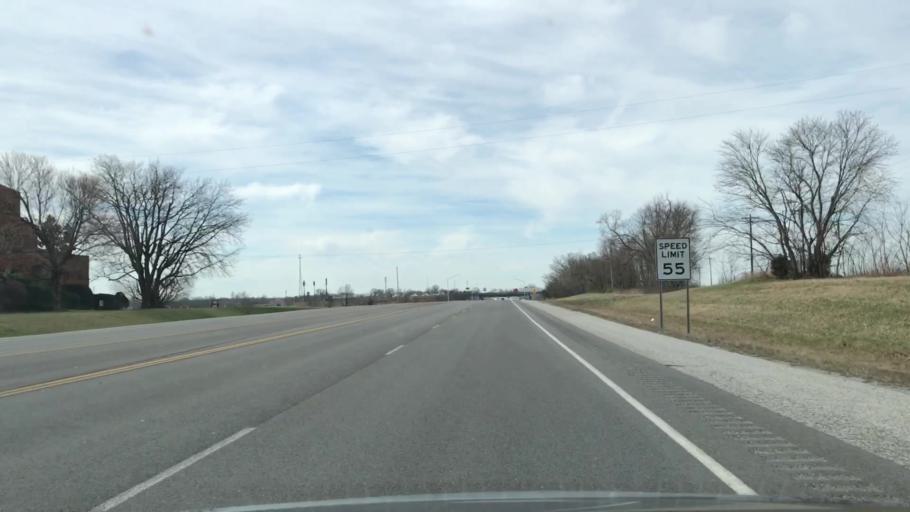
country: US
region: Kentucky
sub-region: Trigg County
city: Cadiz
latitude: 36.8857
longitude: -87.7301
